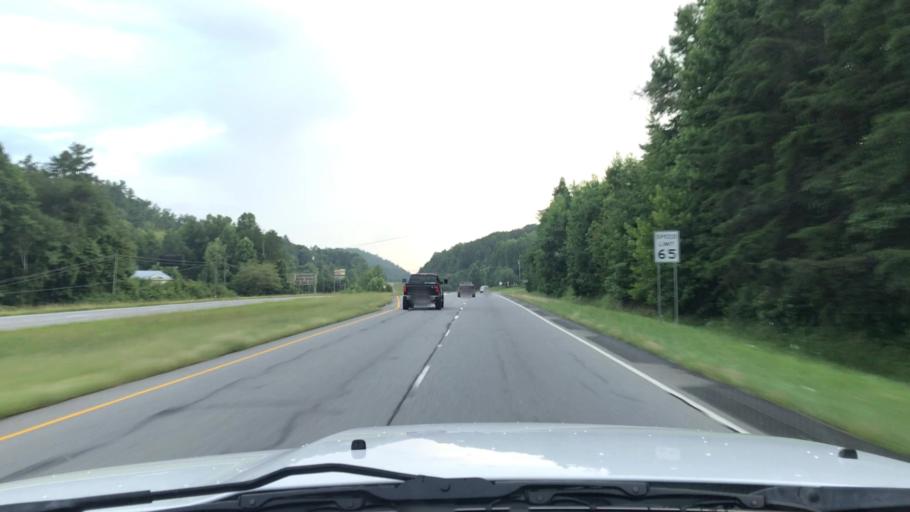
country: US
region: Georgia
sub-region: Fannin County
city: Blue Ridge
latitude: 34.8245
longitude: -84.3588
